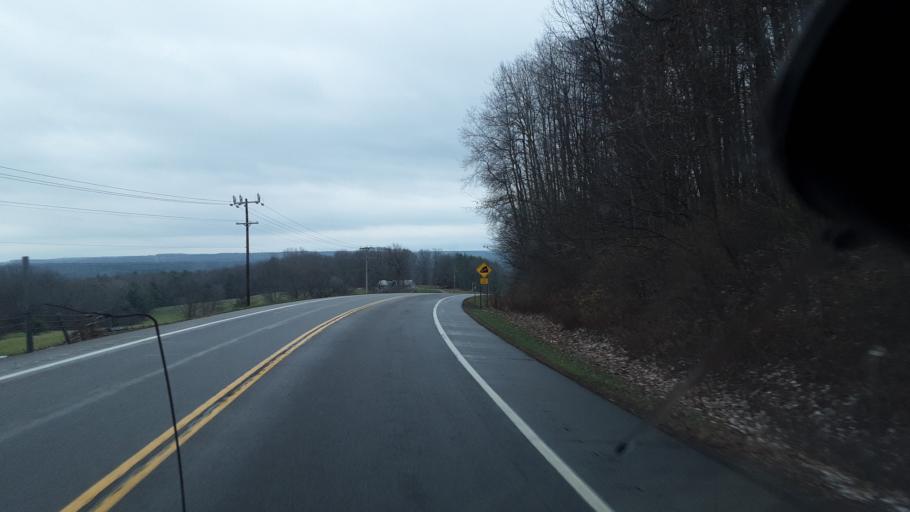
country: US
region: New York
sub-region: Allegany County
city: Houghton
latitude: 42.3935
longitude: -78.1727
